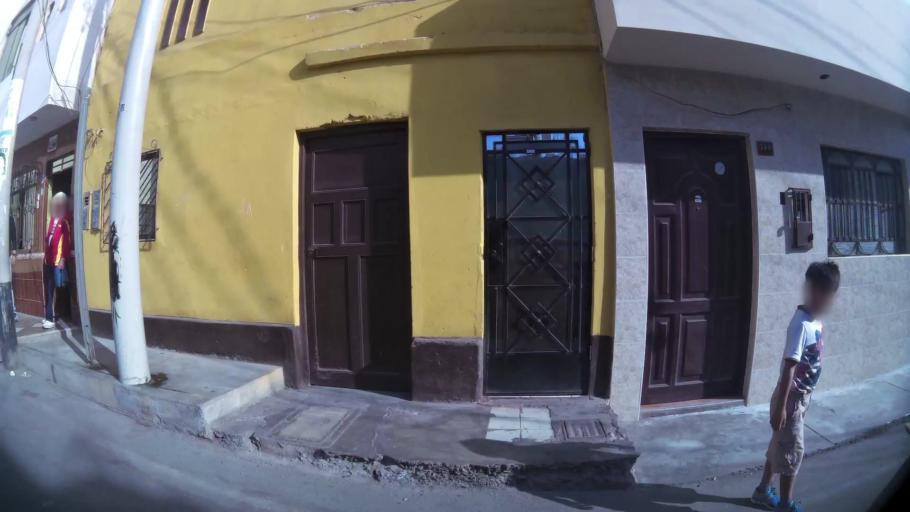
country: PE
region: Lima
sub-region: Huaura
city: Huacho
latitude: -11.1127
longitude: -77.6106
